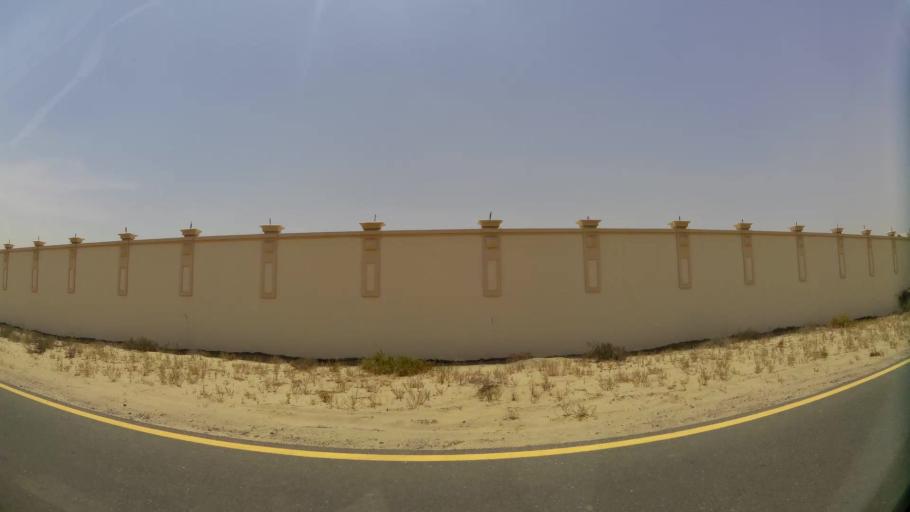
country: AE
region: Ash Shariqah
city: Sharjah
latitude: 25.2443
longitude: 55.4704
